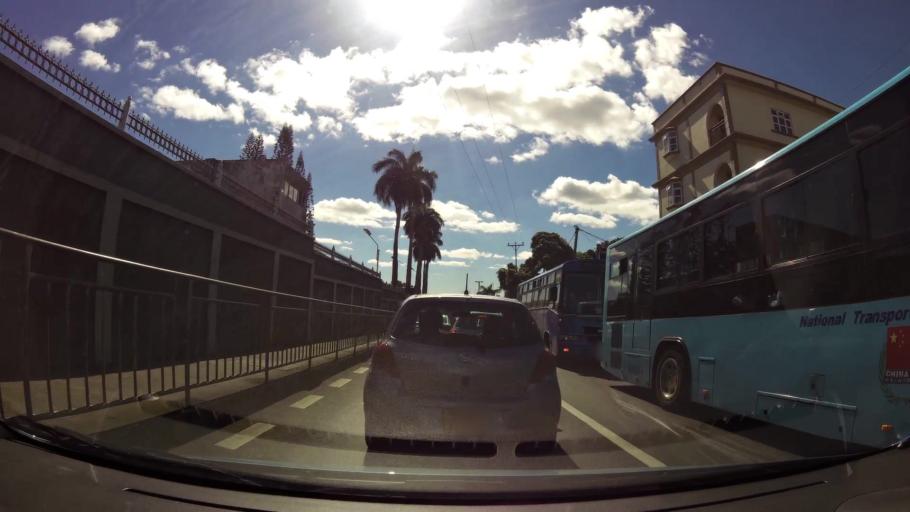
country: MU
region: Plaines Wilhems
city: Quatre Bornes
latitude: -20.2779
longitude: 57.4775
